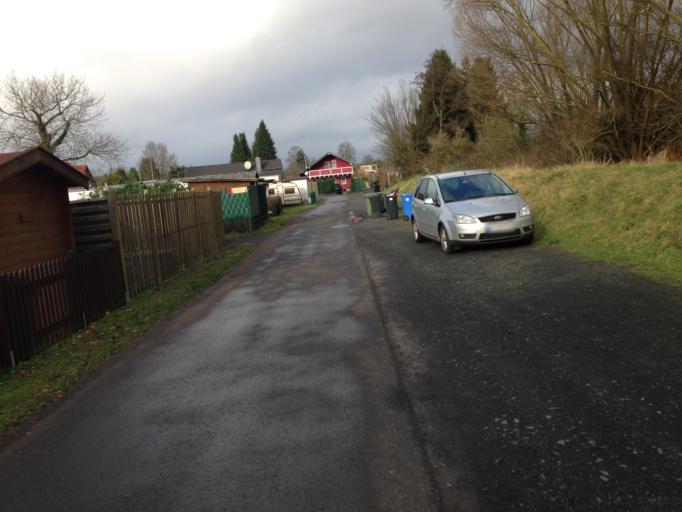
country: DE
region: Hesse
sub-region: Regierungsbezirk Giessen
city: Hungen
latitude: 50.4549
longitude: 8.9080
